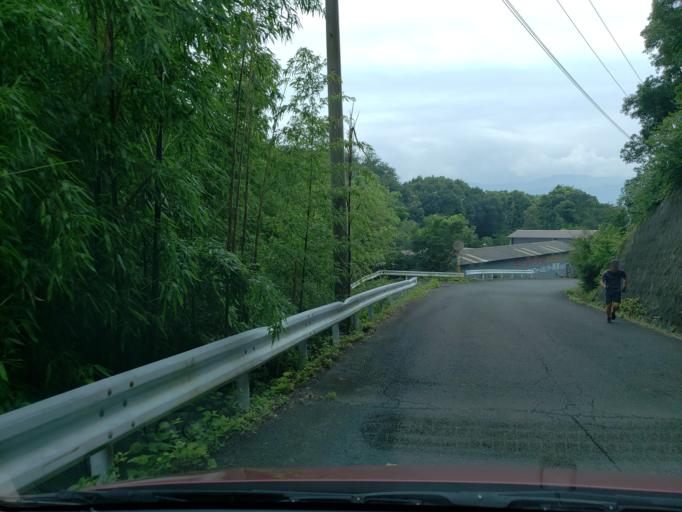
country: JP
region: Tokushima
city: Kamojimacho-jogejima
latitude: 34.1080
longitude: 134.2983
